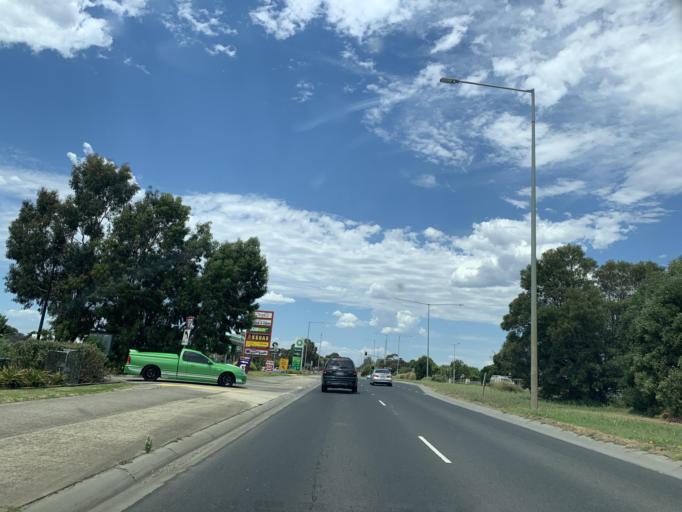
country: AU
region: Victoria
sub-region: Casey
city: Cranbourne West
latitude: -38.1105
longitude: 145.2631
